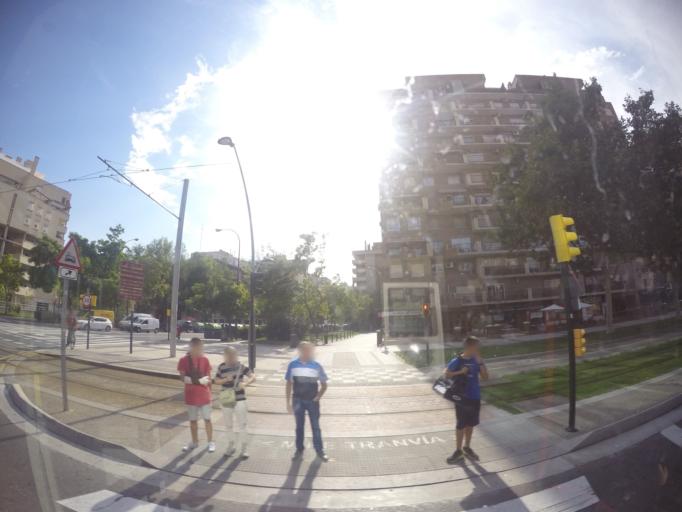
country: ES
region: Aragon
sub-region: Provincia de Zaragoza
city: Almozara
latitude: 41.6690
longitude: -0.8897
